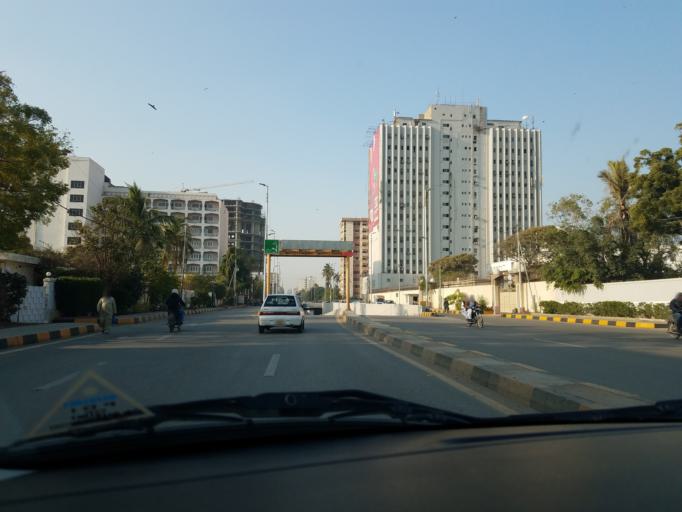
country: PK
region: Sindh
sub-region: Karachi District
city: Karachi
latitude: 24.8508
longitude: 67.0350
